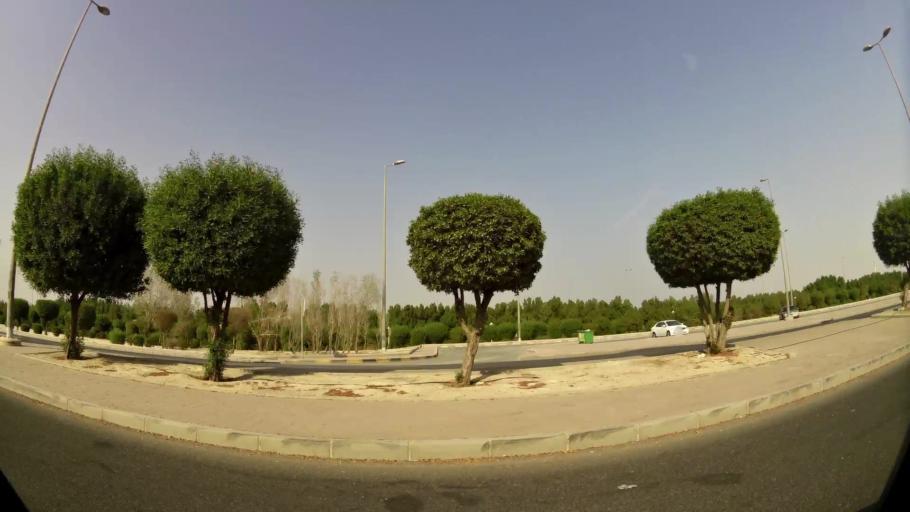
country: KW
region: Muhafazat al Jahra'
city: Al Jahra'
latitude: 29.3451
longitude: 47.7008
